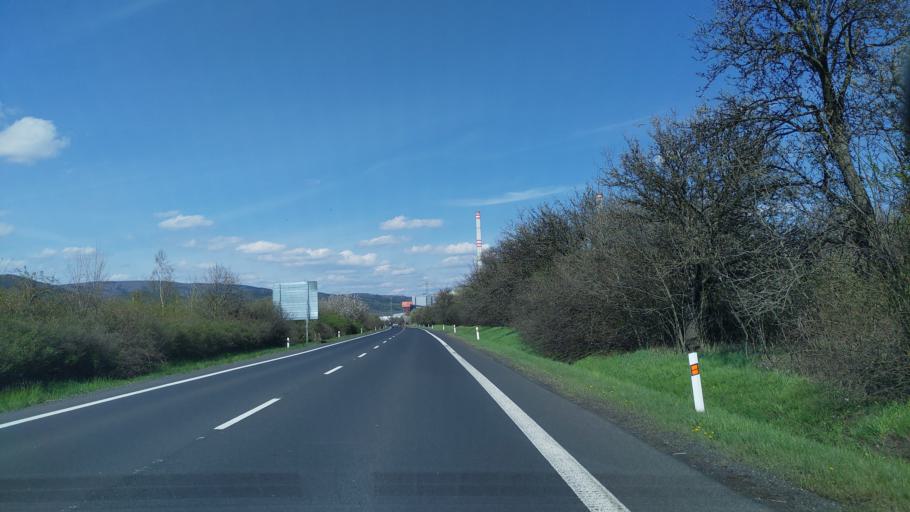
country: CZ
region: Ustecky
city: Kadan
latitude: 50.4063
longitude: 13.2392
